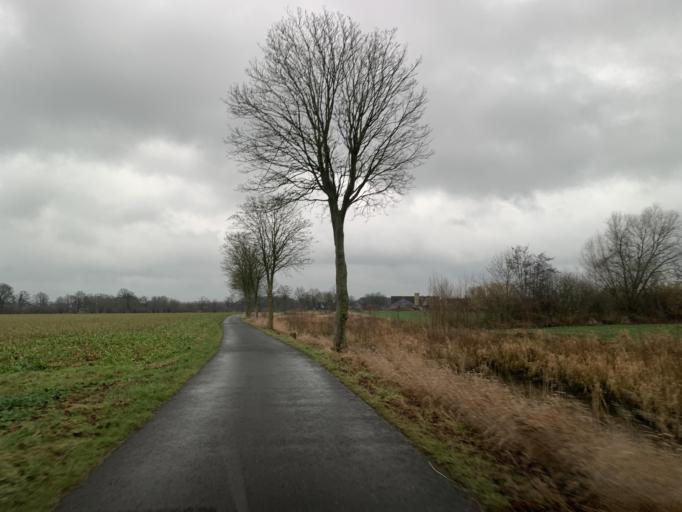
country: DE
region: North Rhine-Westphalia
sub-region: Regierungsbezirk Munster
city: Nordwalde
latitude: 52.0985
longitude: 7.4833
